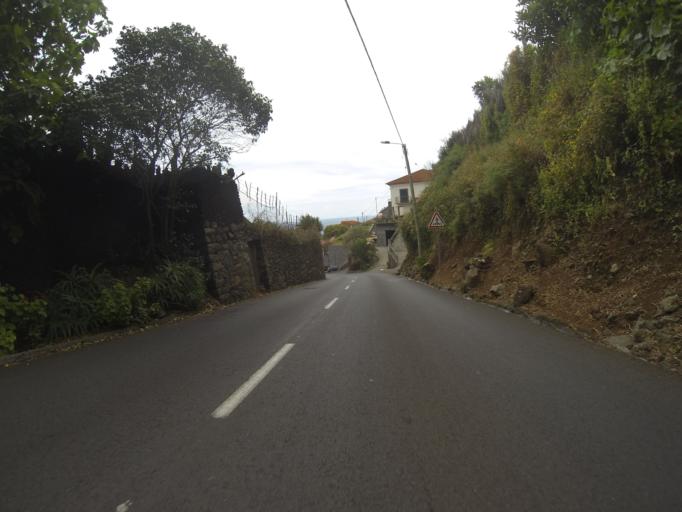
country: PT
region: Madeira
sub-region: Porto Moniz
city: Porto Moniz
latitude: 32.8651
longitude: -17.1689
